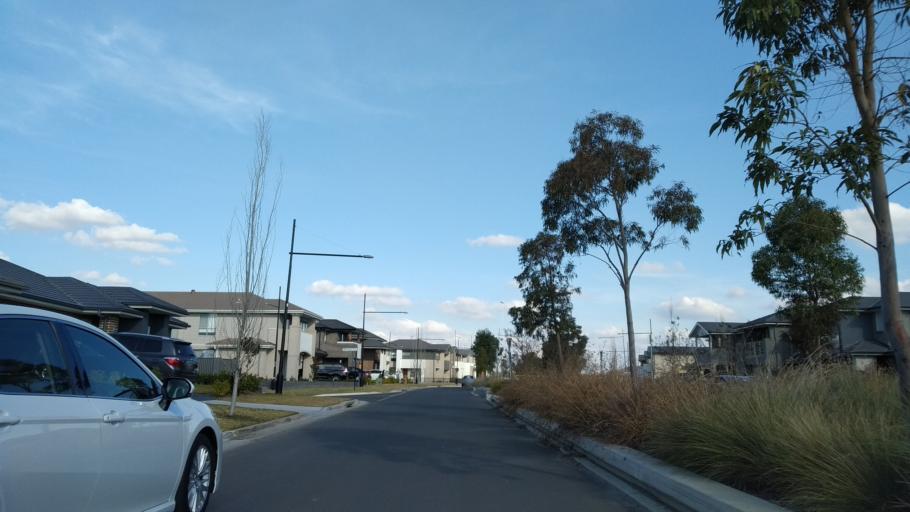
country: AU
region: New South Wales
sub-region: Blacktown
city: Hassall Grove
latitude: -33.6937
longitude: 150.8161
